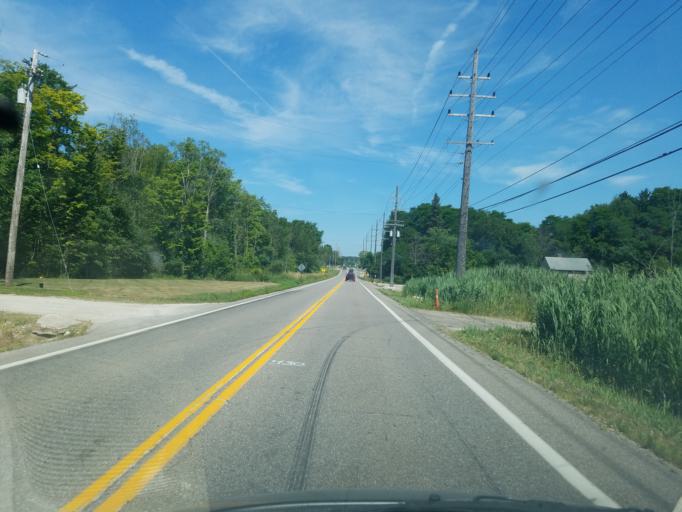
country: US
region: Ohio
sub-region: Geauga County
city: Burton
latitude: 41.5339
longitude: -81.1839
